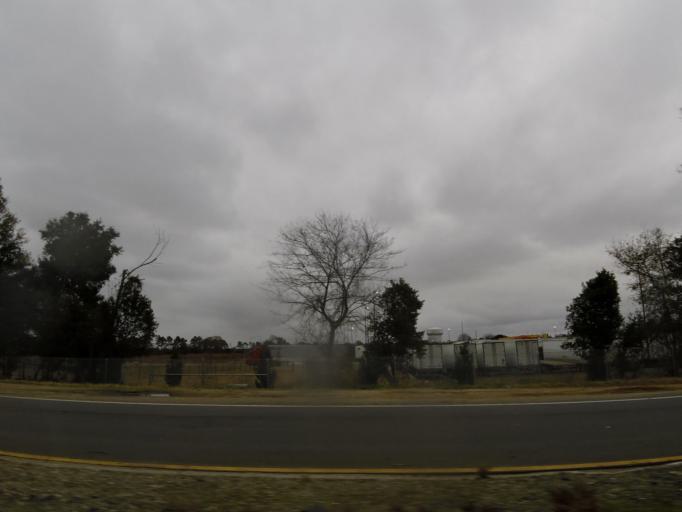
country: US
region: Georgia
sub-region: Dougherty County
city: Albany
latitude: 31.5814
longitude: -84.1098
